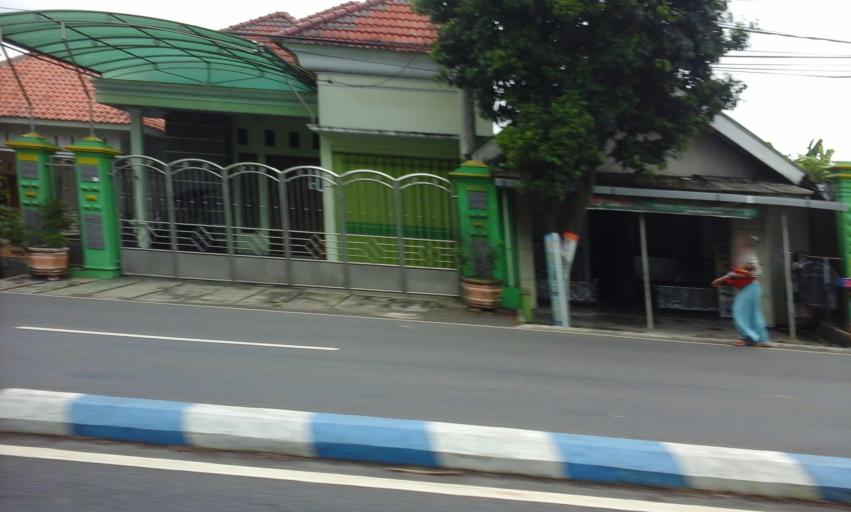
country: ID
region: East Java
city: Krajan Wetan
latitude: -8.0850
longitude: 113.2379
